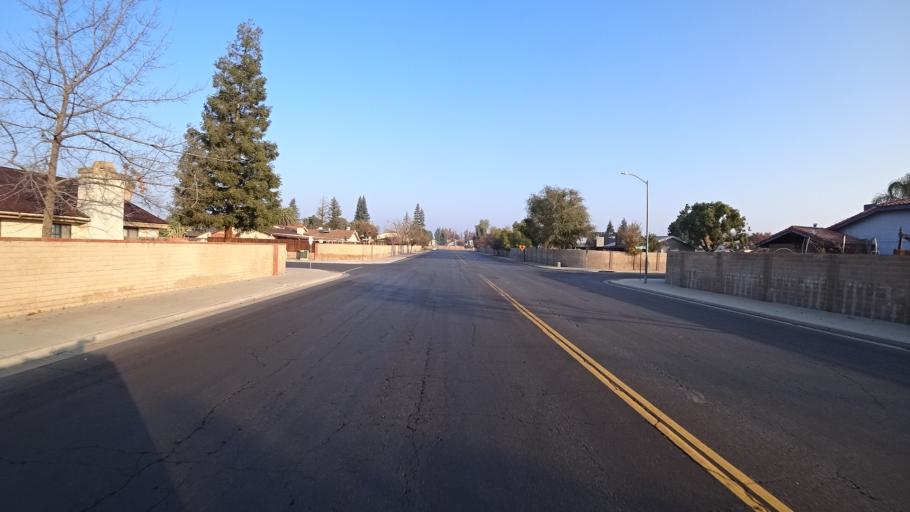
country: US
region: California
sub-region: Kern County
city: Greenacres
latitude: 35.3209
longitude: -119.0835
